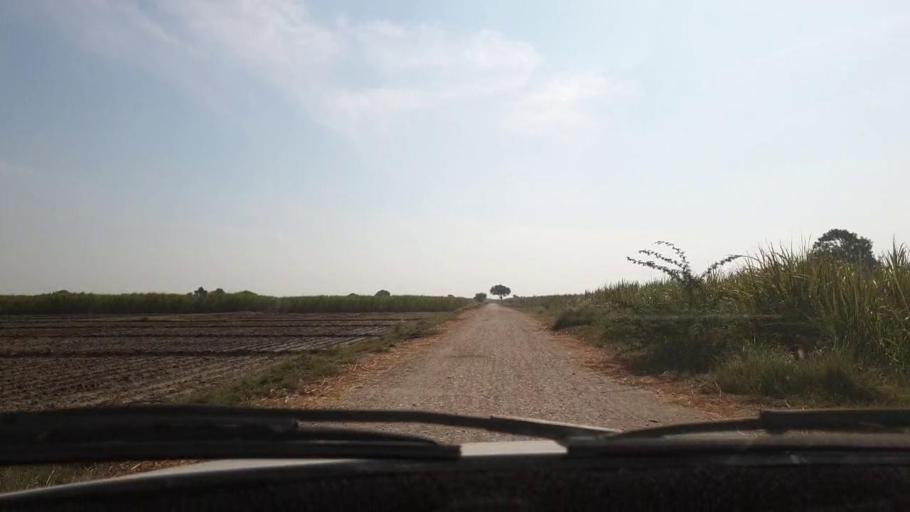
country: PK
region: Sindh
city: Bulri
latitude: 24.9558
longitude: 68.4445
